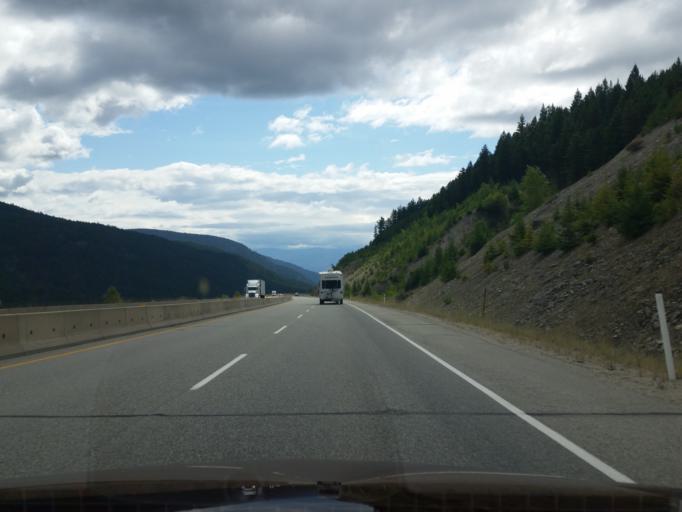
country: CA
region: British Columbia
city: Peachland
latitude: 49.8610
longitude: -119.8541
